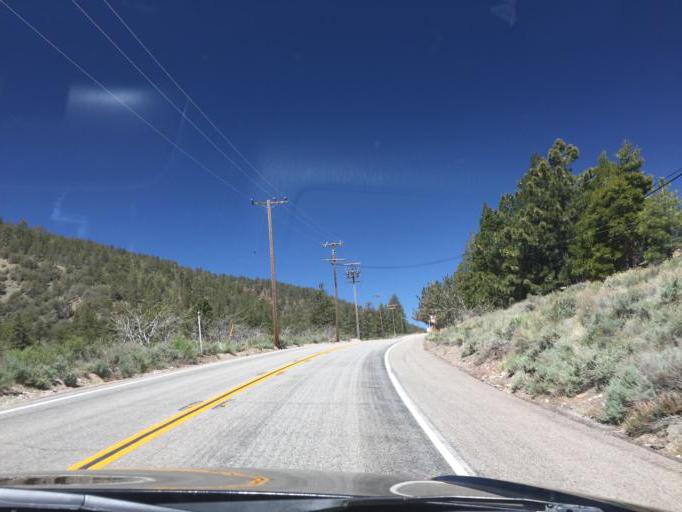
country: US
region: California
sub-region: San Bernardino County
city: Wrightwood
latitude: 34.3678
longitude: -117.6596
